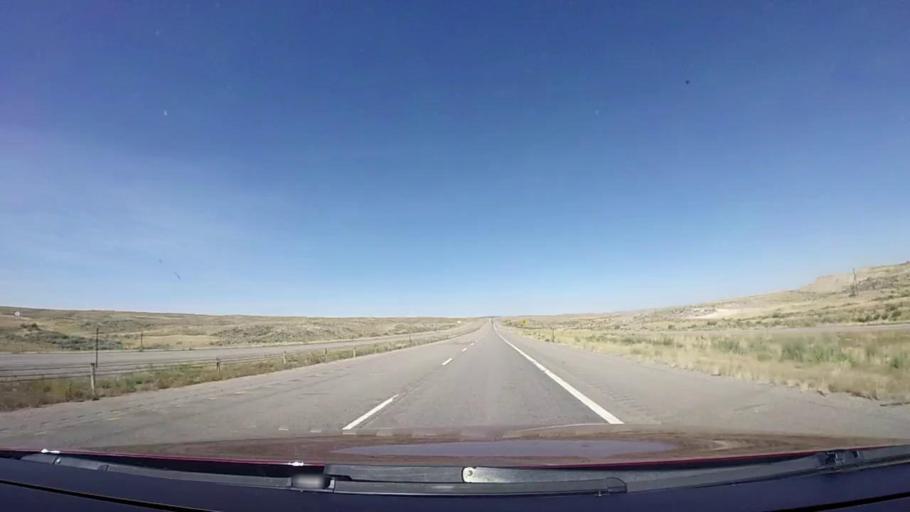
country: US
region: Wyoming
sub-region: Sweetwater County
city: Rock Springs
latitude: 41.6476
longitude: -108.6828
